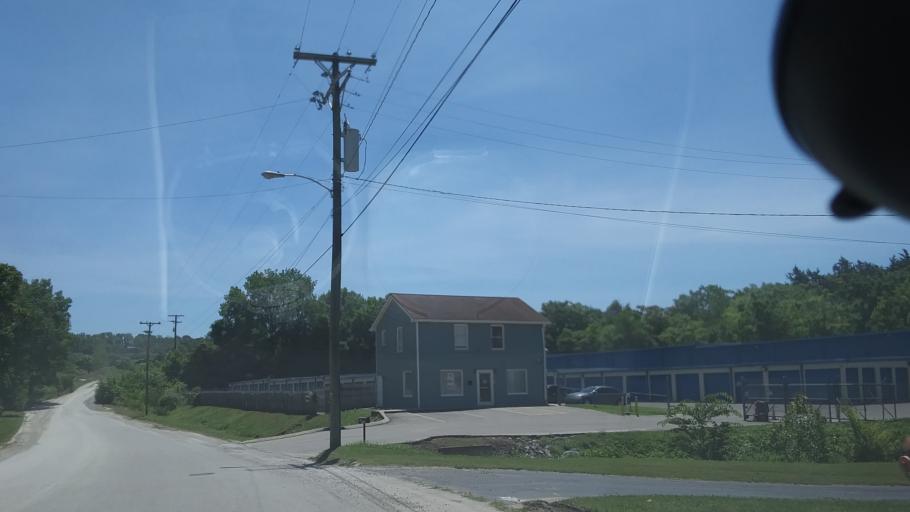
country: US
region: Tennessee
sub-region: Davidson County
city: Oak Hill
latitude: 36.0918
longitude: -86.6741
